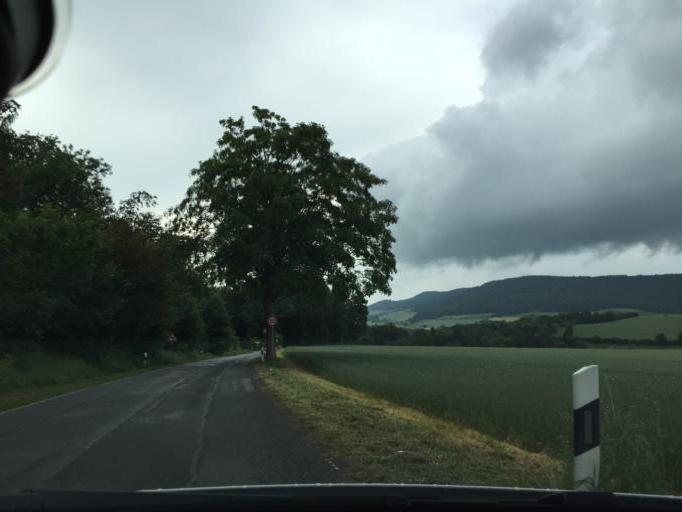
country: DE
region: Lower Saxony
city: Ottenstein
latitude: 51.9978
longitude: 9.3555
